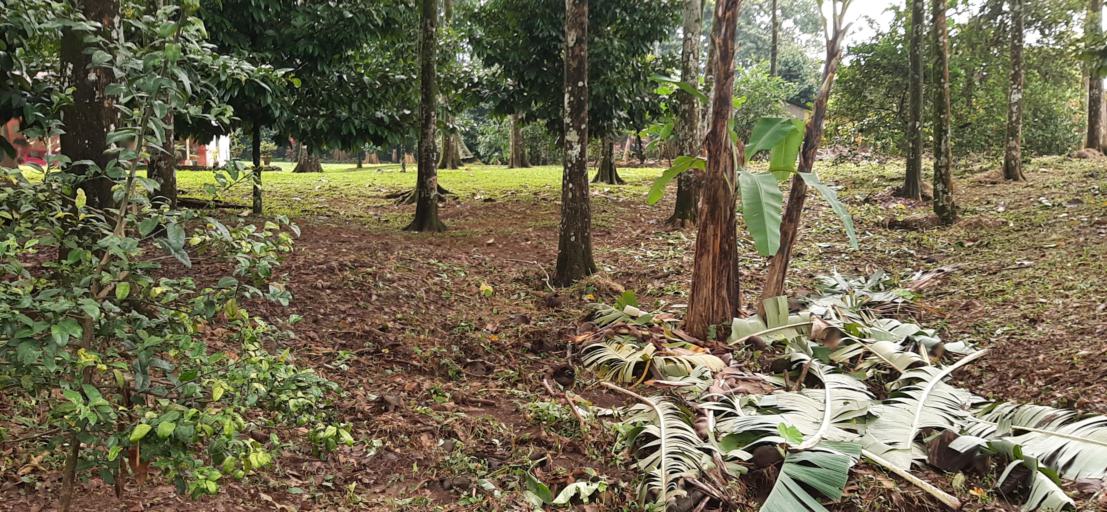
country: GT
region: Retalhuleu
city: San Felipe
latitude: 14.6100
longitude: -91.5772
